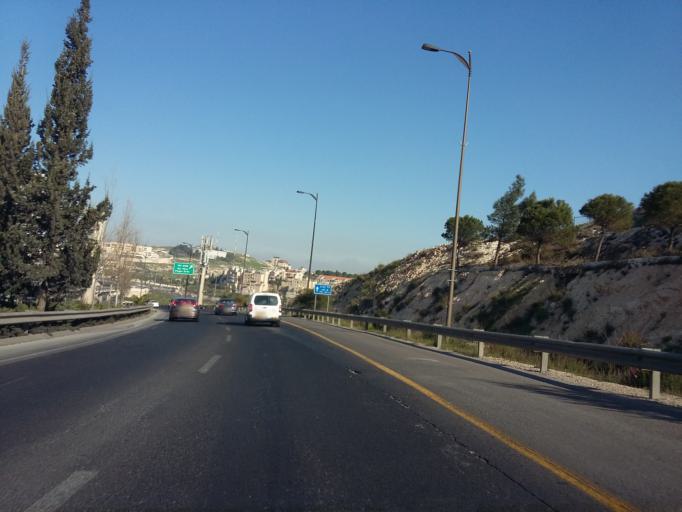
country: PS
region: West Bank
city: `Anata
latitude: 31.8147
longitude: 35.2383
